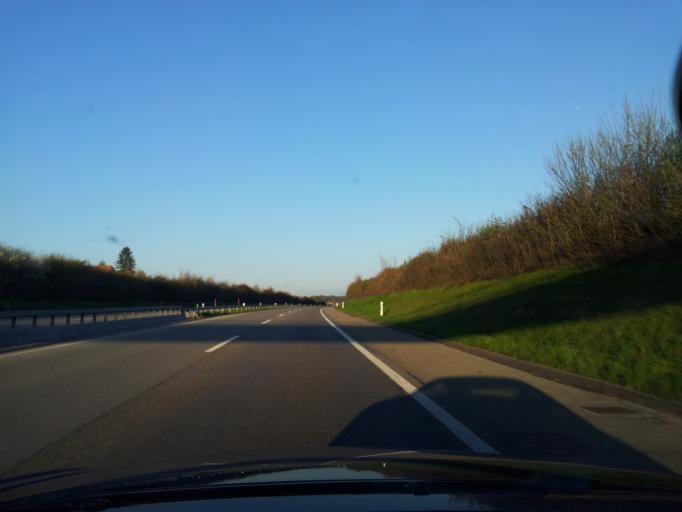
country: CH
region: Bern
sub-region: Seeland District
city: Grossaffoltern
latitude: 47.0496
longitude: 7.3638
